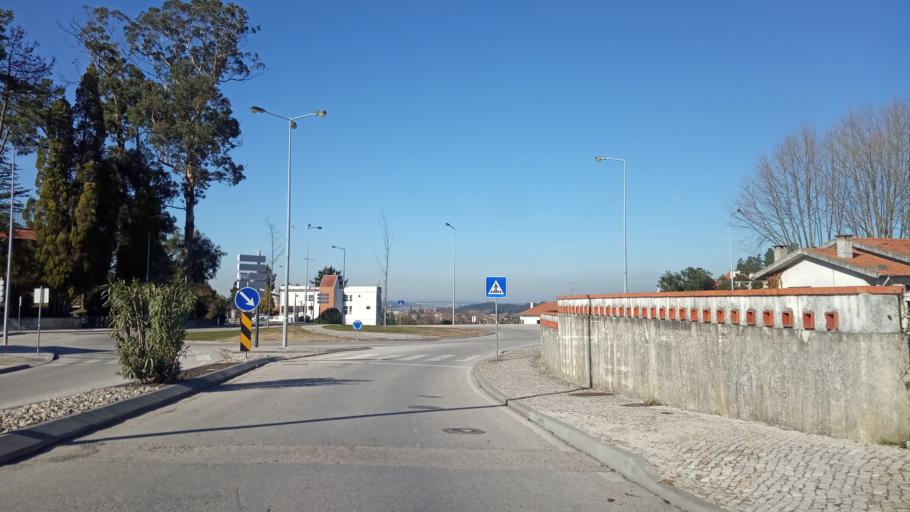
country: PT
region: Aveiro
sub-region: Anadia
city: Arcos
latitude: 40.4395
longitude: -8.4437
